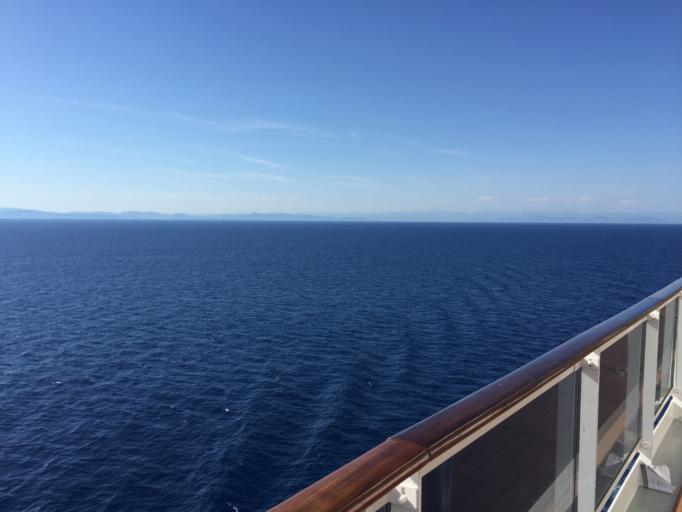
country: FR
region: Provence-Alpes-Cote d'Azur
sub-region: Departement du Var
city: Ramatuelle
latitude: 43.0651
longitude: 6.8452
